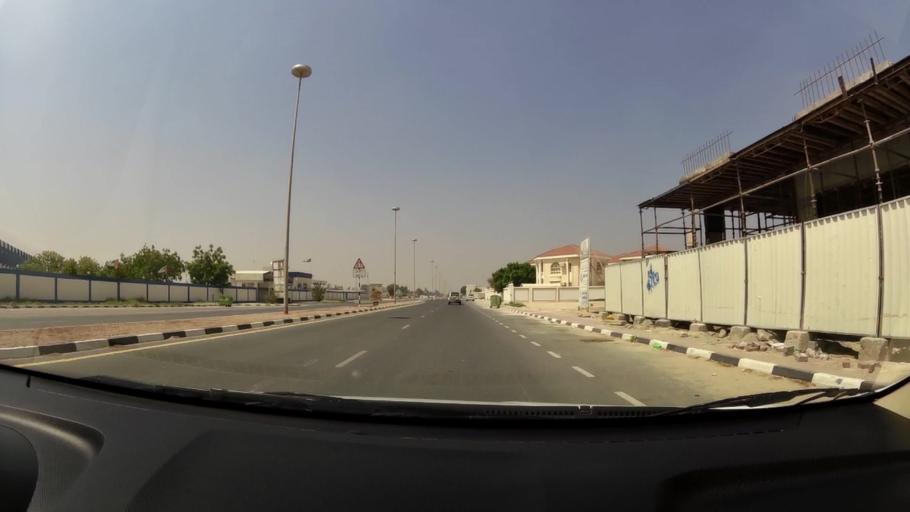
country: AE
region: Umm al Qaywayn
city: Umm al Qaywayn
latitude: 25.5674
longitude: 55.5581
